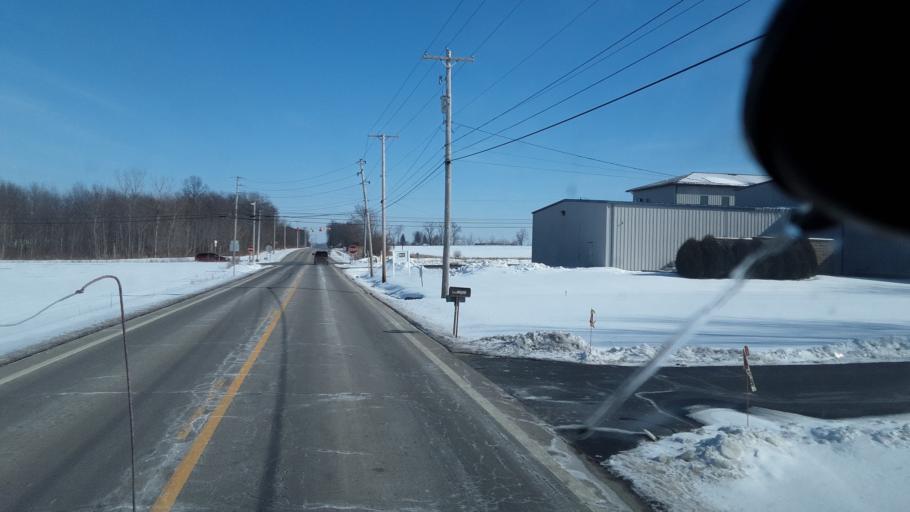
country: US
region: Ohio
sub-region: Columbiana County
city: Salem
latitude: 40.9444
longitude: -80.8578
